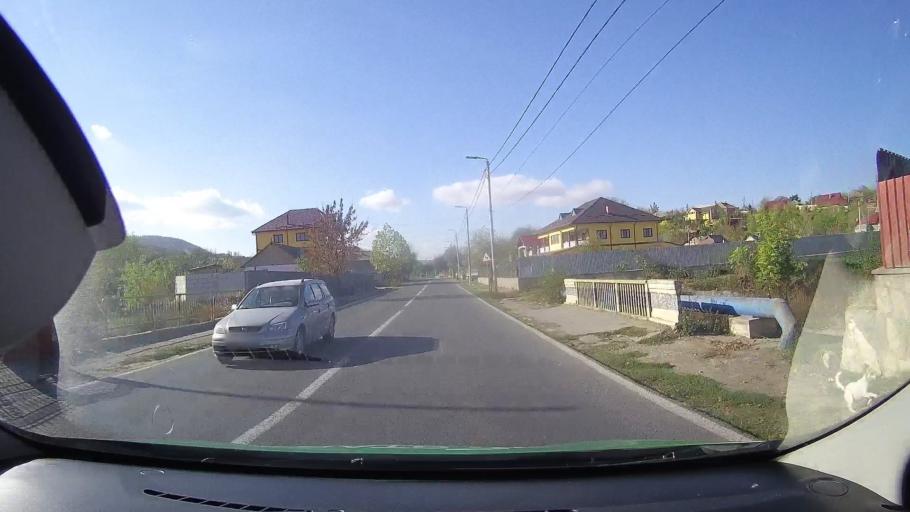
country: RO
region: Tulcea
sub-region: Oras Babadag
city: Babadag
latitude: 44.8903
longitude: 28.7130
